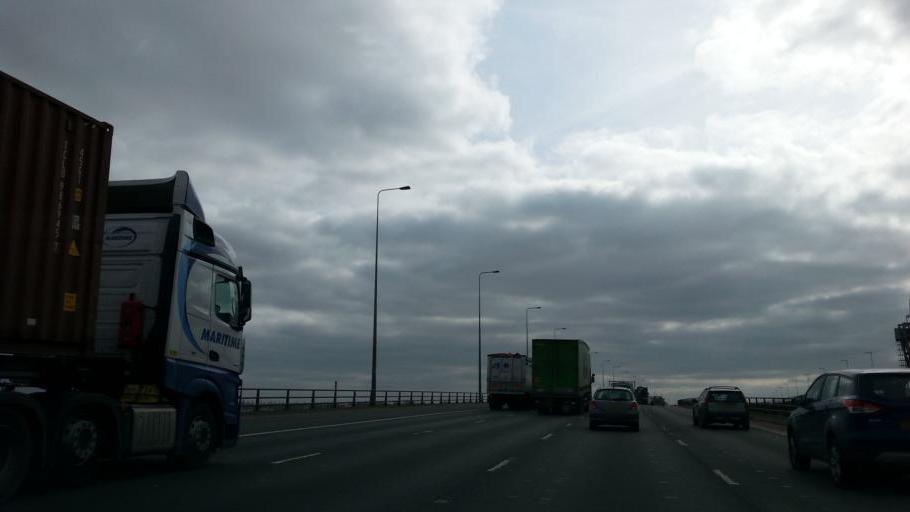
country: GB
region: England
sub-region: Warrington
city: Lymm
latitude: 53.3916
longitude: -2.5059
